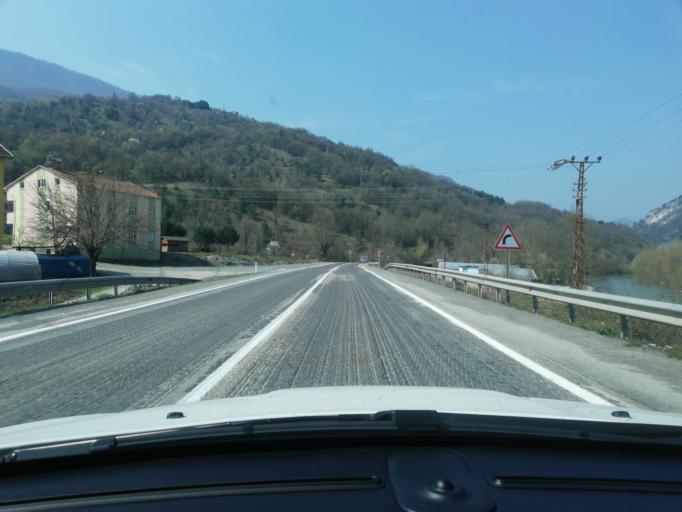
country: TR
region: Karabuk
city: Yenice
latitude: 41.2150
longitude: 32.2545
